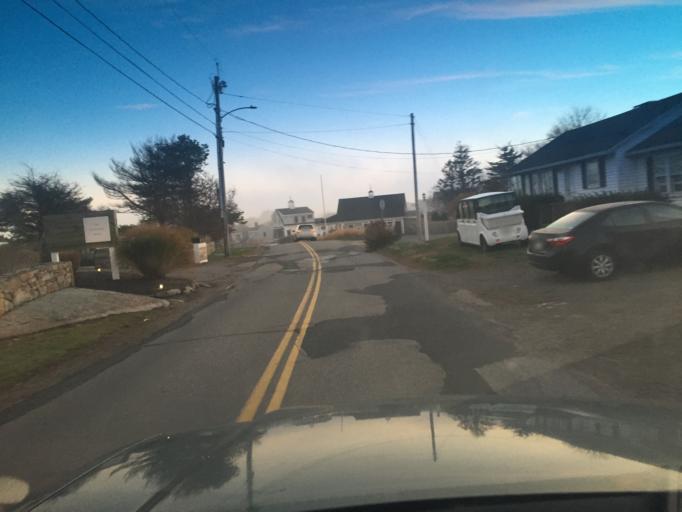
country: US
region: Maine
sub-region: York County
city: York Beach
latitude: 43.1687
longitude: -70.5957
